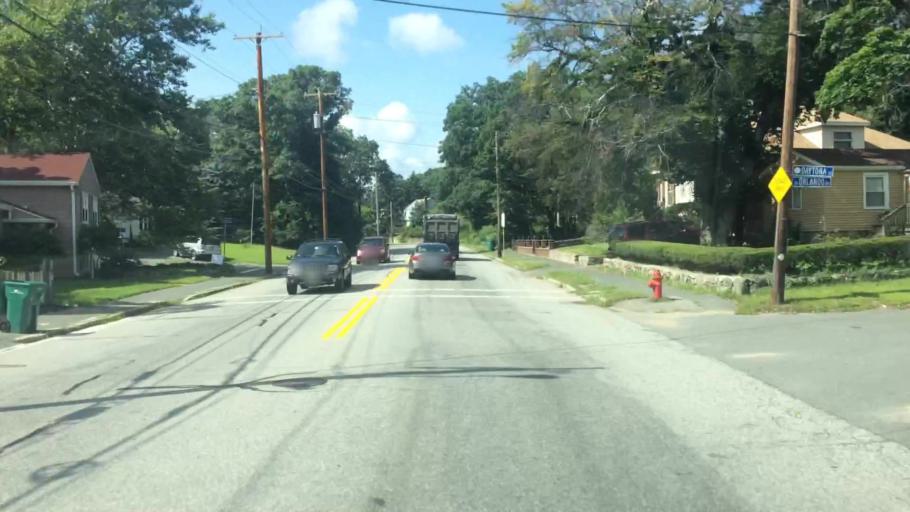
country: US
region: Massachusetts
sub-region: Essex County
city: South Peabody
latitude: 42.5033
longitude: -70.9802
